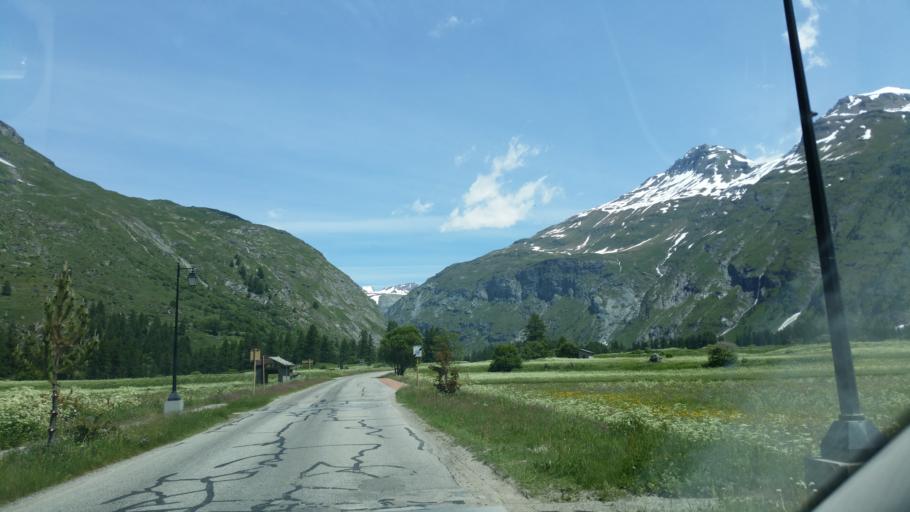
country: IT
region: Piedmont
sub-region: Provincia di Torino
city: Moncenisio
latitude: 45.3240
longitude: 7.0021
